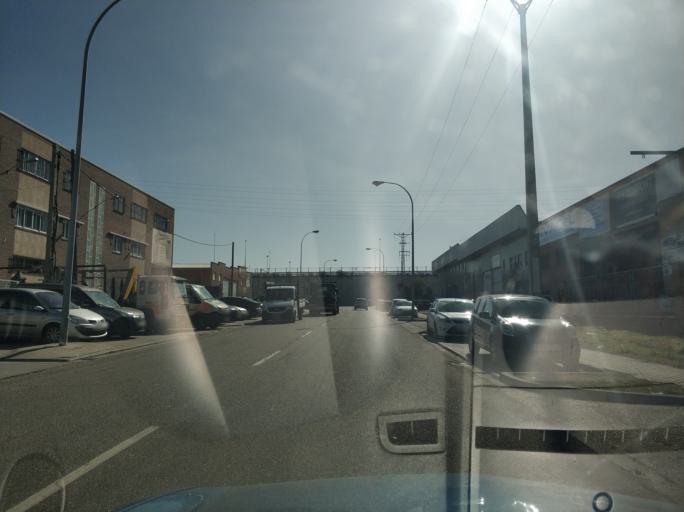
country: ES
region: Castille and Leon
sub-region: Provincia de Valladolid
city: Cisterniga
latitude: 41.6213
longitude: -4.6973
